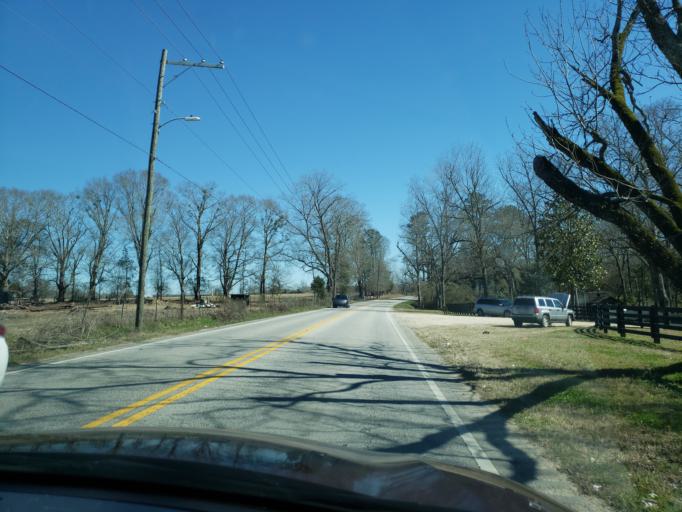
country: US
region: Alabama
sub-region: Lee County
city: Auburn
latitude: 32.6041
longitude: -85.5906
